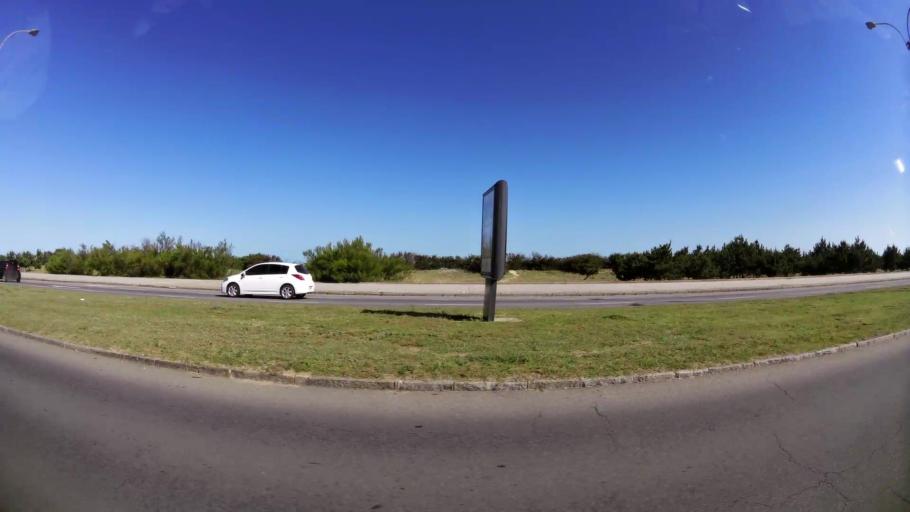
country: UY
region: Canelones
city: Barra de Carrasco
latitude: -34.8835
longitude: -56.0384
